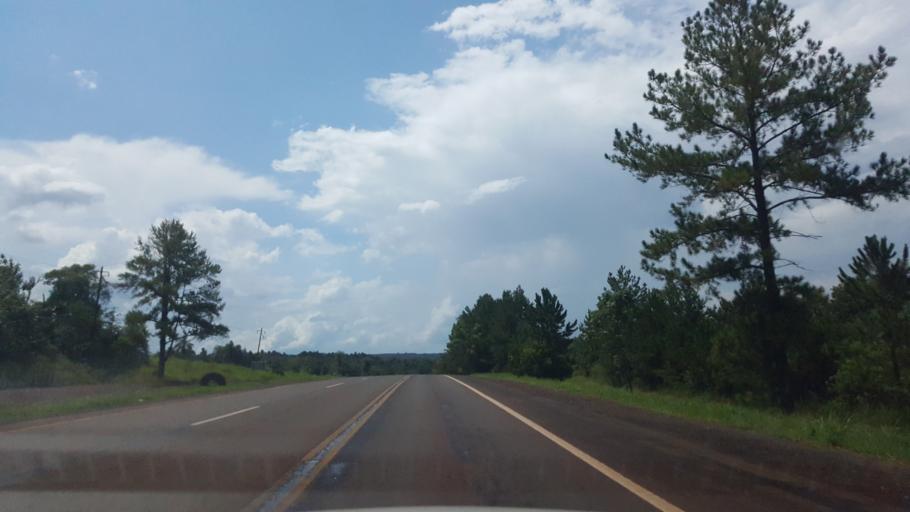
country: AR
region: Misiones
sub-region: Departamento de Eldorado
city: Eldorado
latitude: -26.3664
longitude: -54.6226
